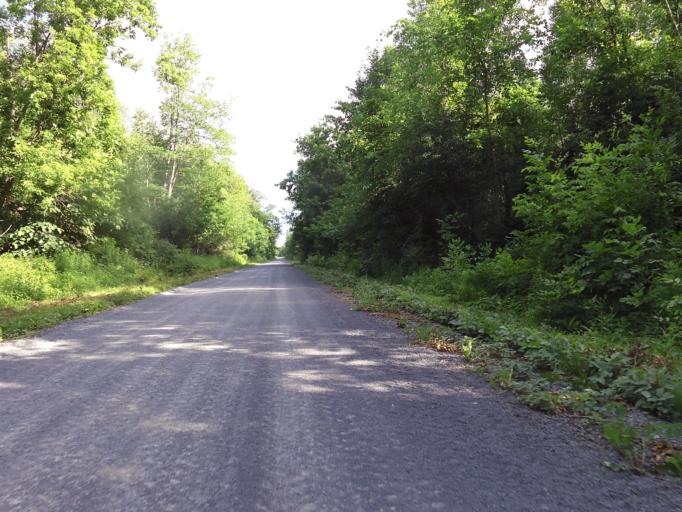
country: CA
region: Ontario
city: Arnprior
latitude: 45.3233
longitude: -76.2874
